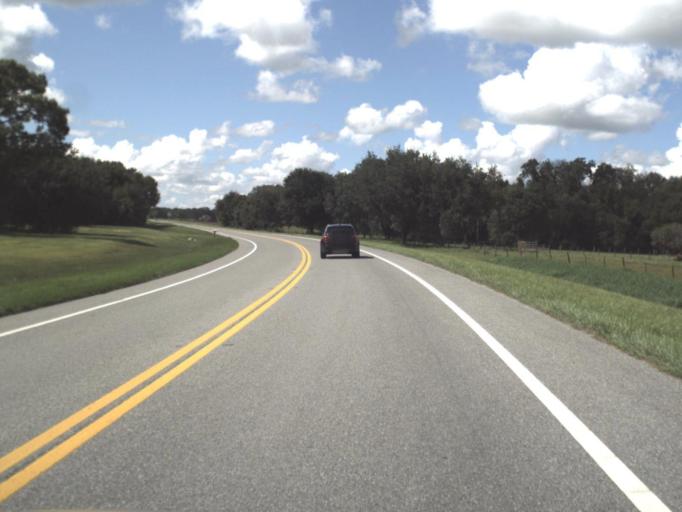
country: US
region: Florida
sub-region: Sarasota County
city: Warm Mineral Springs
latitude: 27.3357
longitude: -82.1366
